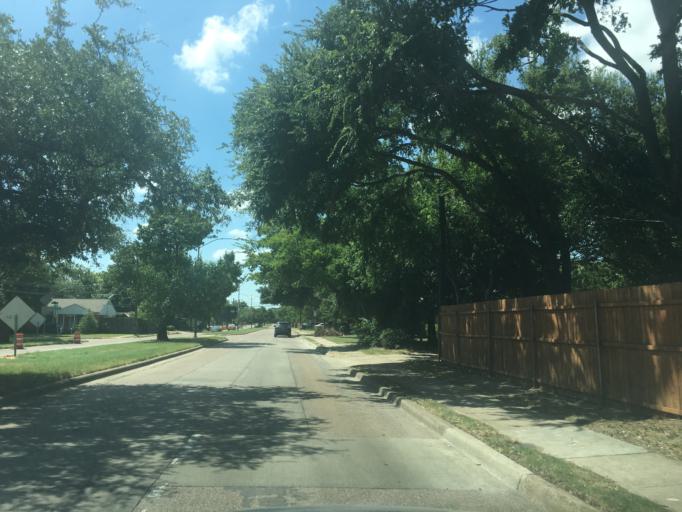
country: US
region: Texas
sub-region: Dallas County
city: Garland
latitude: 32.8351
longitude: -96.6781
